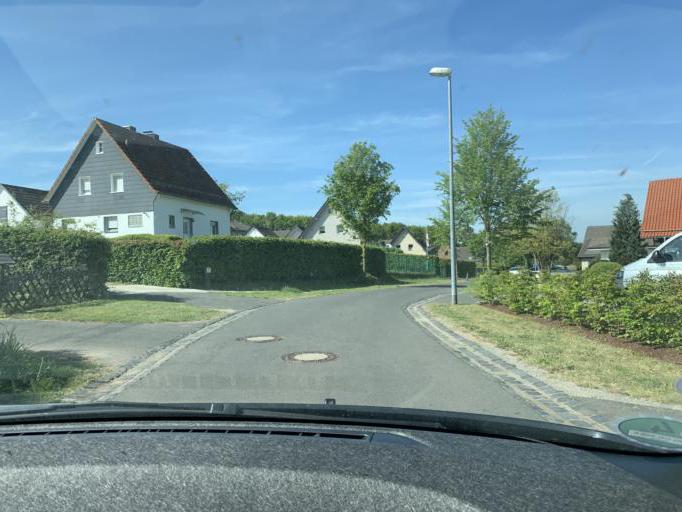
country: DE
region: North Rhine-Westphalia
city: Heimbach
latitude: 50.5898
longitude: 6.4959
